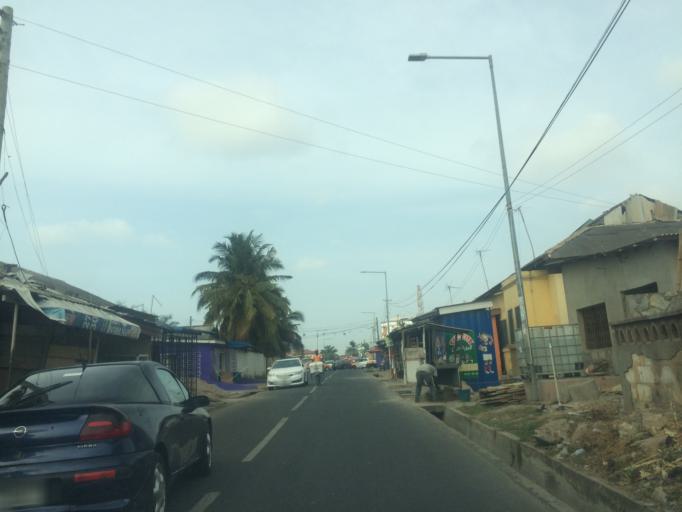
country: GH
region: Greater Accra
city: Accra
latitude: 5.5543
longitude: -0.1795
